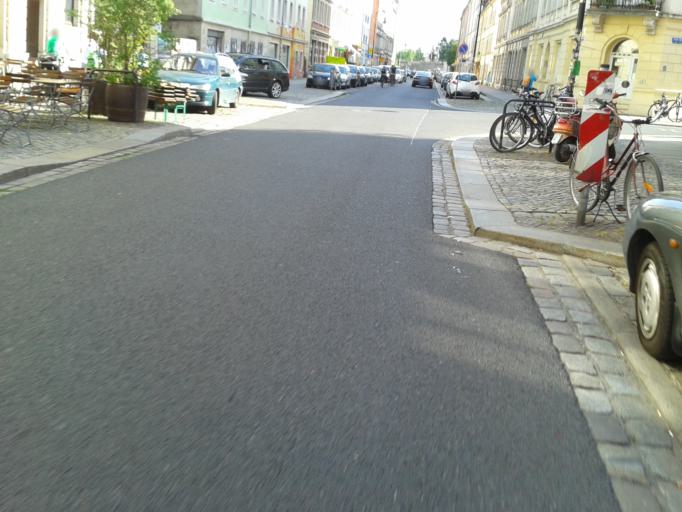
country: DE
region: Saxony
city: Albertstadt
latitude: 51.0737
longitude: 13.7487
